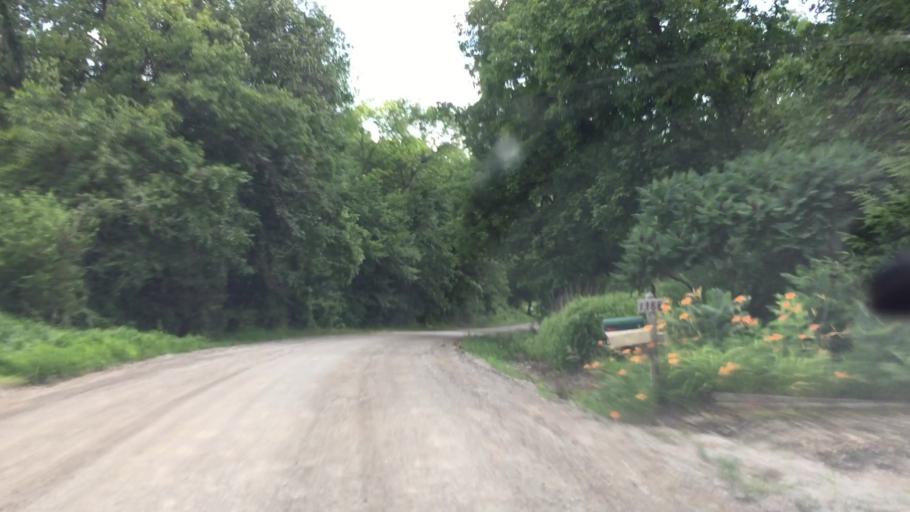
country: US
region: Iowa
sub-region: Linn County
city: Ely
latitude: 41.8344
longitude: -91.6114
